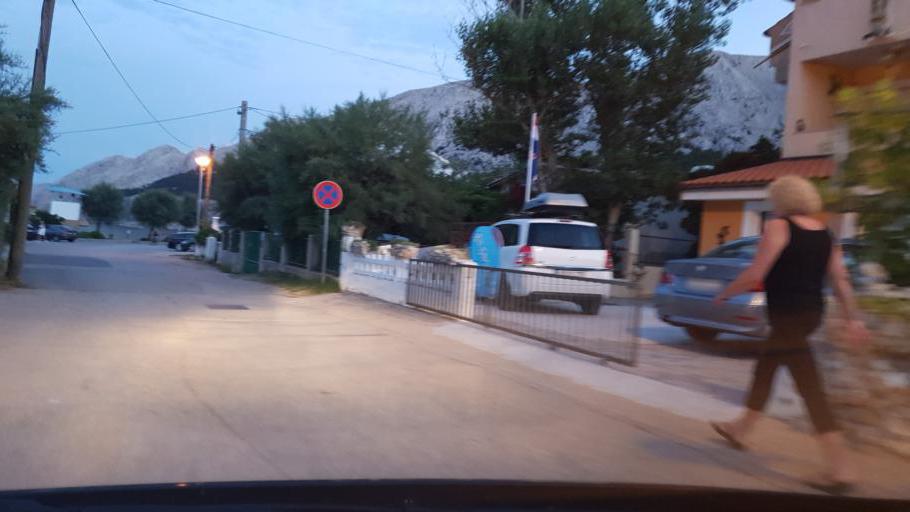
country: HR
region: Primorsko-Goranska
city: Punat
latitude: 44.9624
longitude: 14.7467
